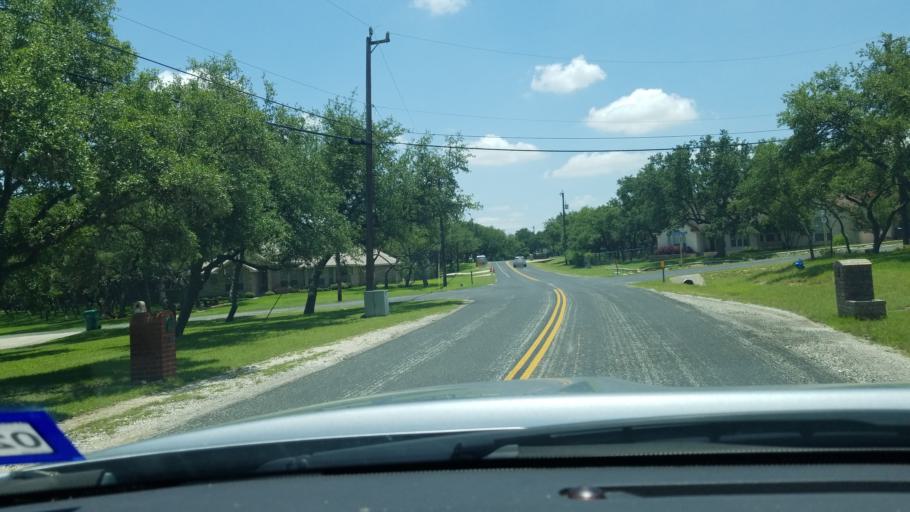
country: US
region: Texas
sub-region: Bexar County
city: Timberwood Park
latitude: 29.7022
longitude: -98.5076
